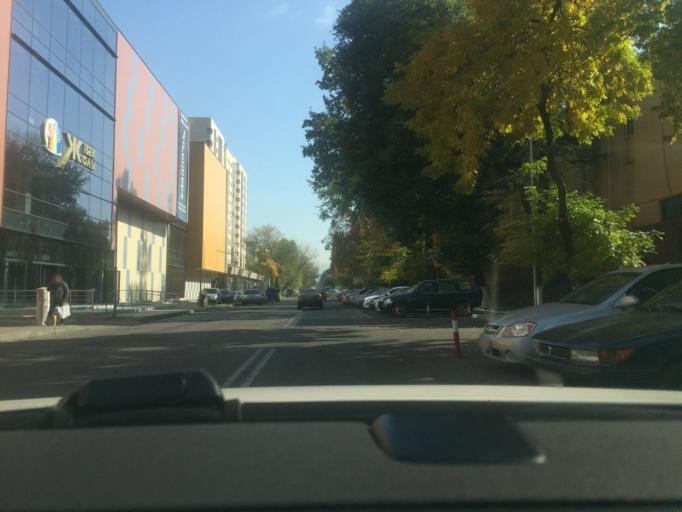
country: KZ
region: Almaty Qalasy
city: Almaty
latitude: 43.2608
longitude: 76.9287
